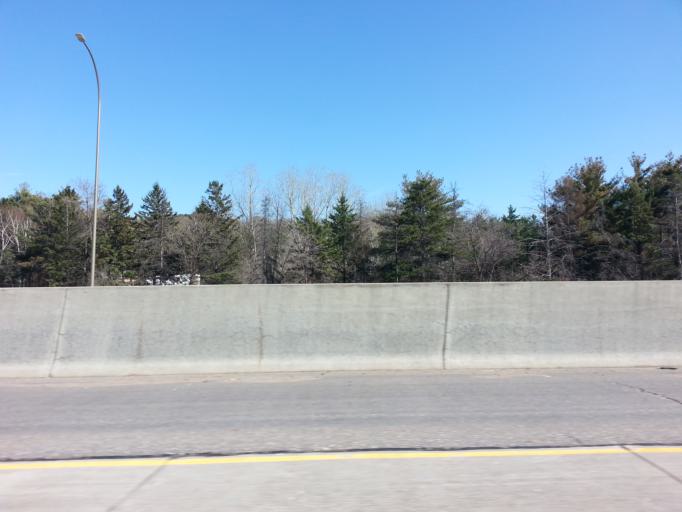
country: US
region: Minnesota
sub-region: Washington County
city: Newport
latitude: 44.8973
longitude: -92.9967
